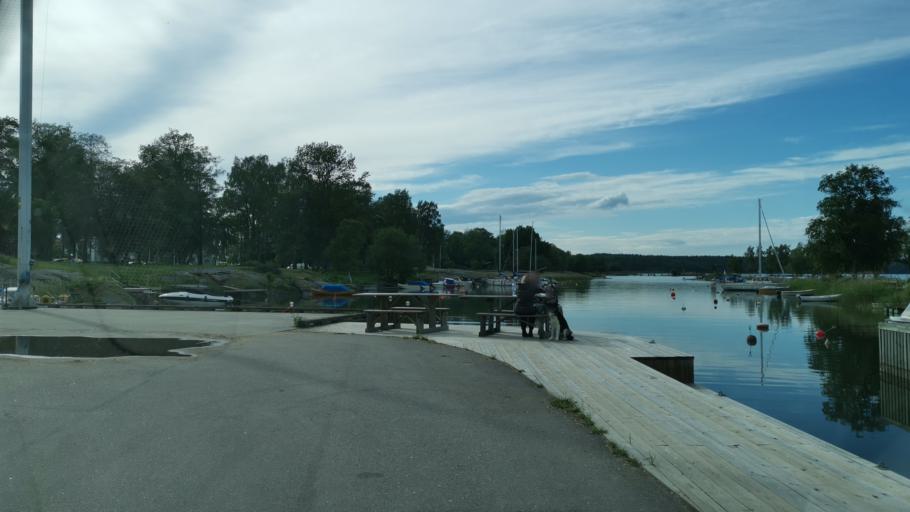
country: SE
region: Vaestra Goetaland
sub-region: Vanersborgs Kommun
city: Vanersborg
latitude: 58.3832
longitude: 12.3338
